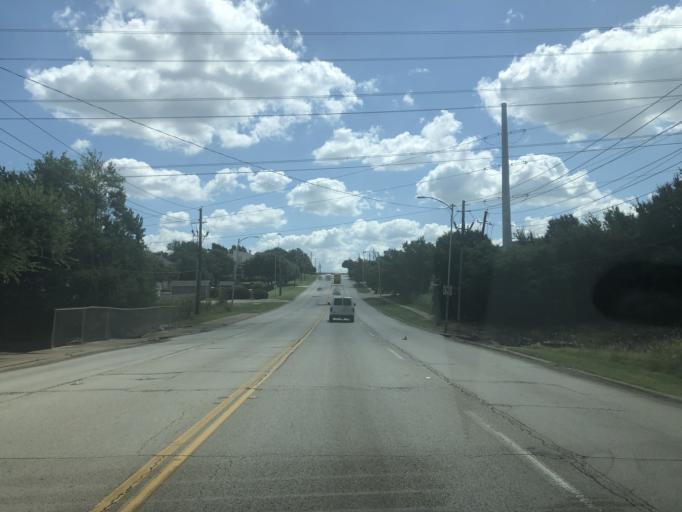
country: US
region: Texas
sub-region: Dallas County
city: Grand Prairie
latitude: 32.7571
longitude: -97.0350
